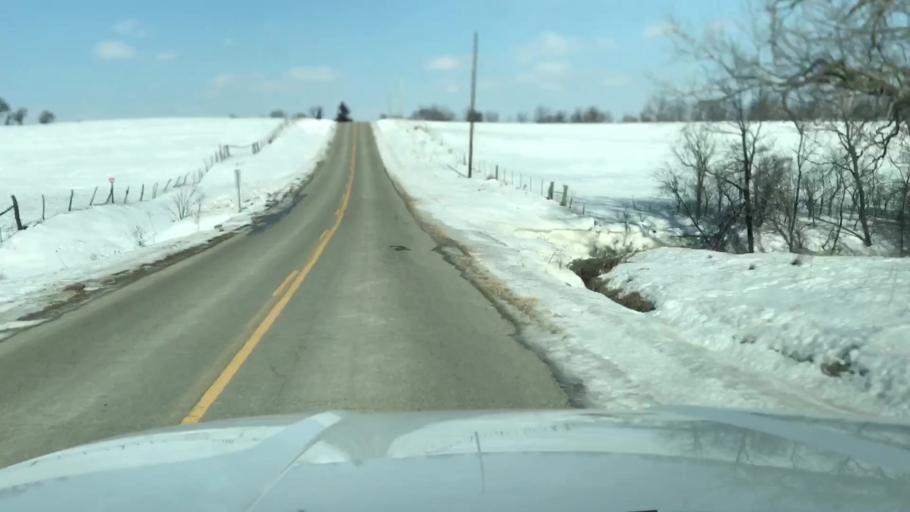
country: US
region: Missouri
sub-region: Nodaway County
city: Maryville
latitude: 40.3766
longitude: -94.7215
